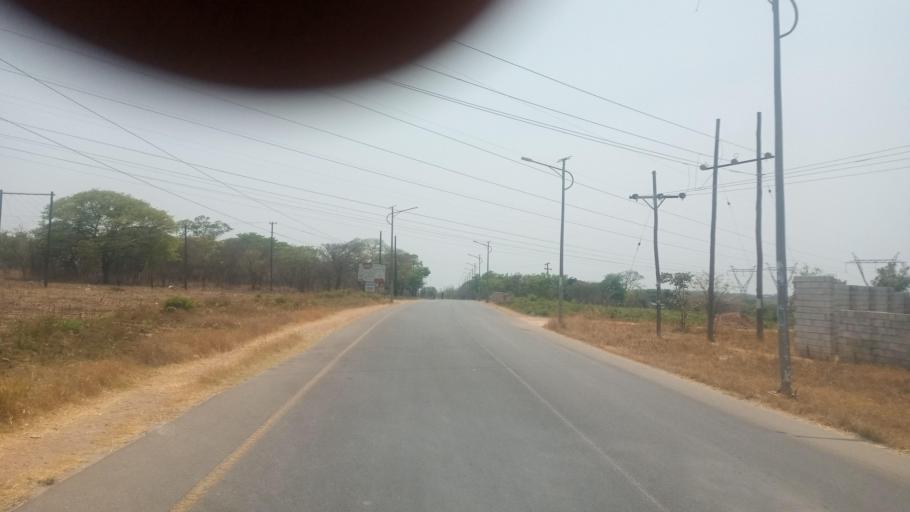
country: ZM
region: Lusaka
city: Lusaka
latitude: -15.4685
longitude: 28.4286
